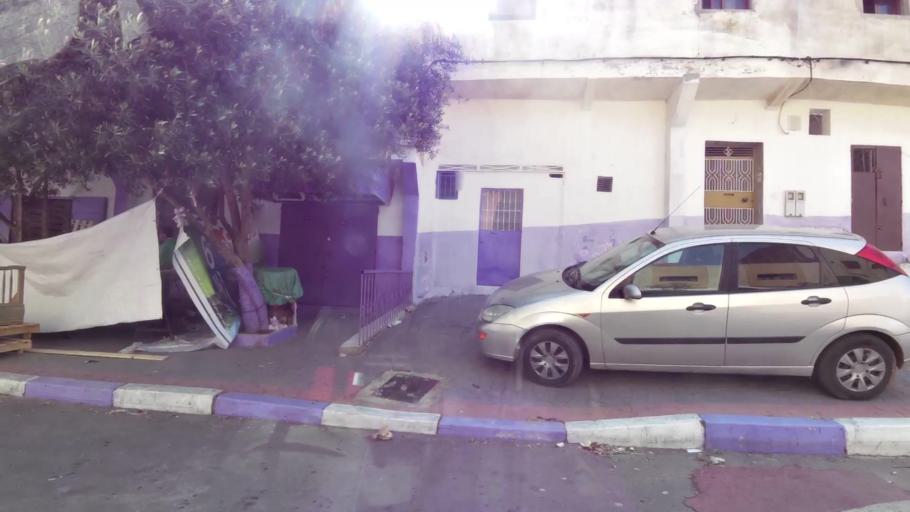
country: MA
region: Tanger-Tetouan
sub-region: Tanger-Assilah
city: Tangier
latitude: 35.7407
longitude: -5.8043
